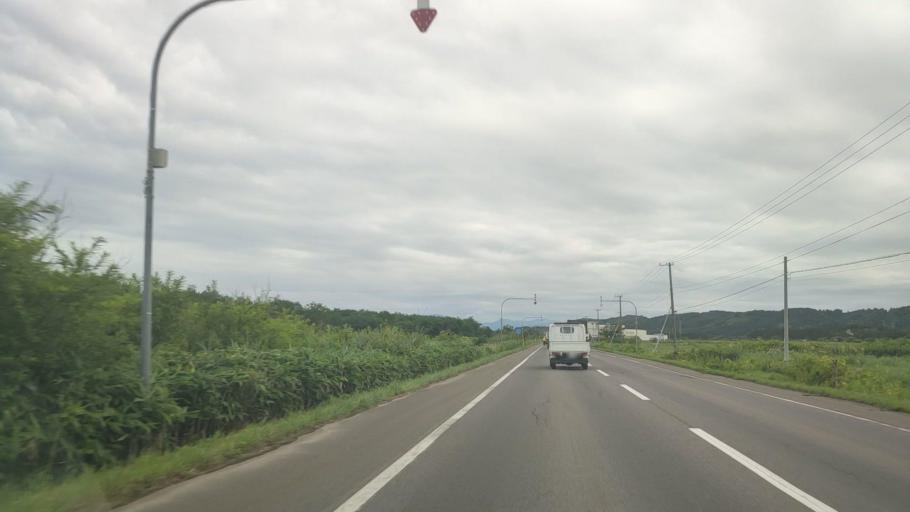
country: JP
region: Hokkaido
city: Niseko Town
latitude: 42.3922
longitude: 140.2990
